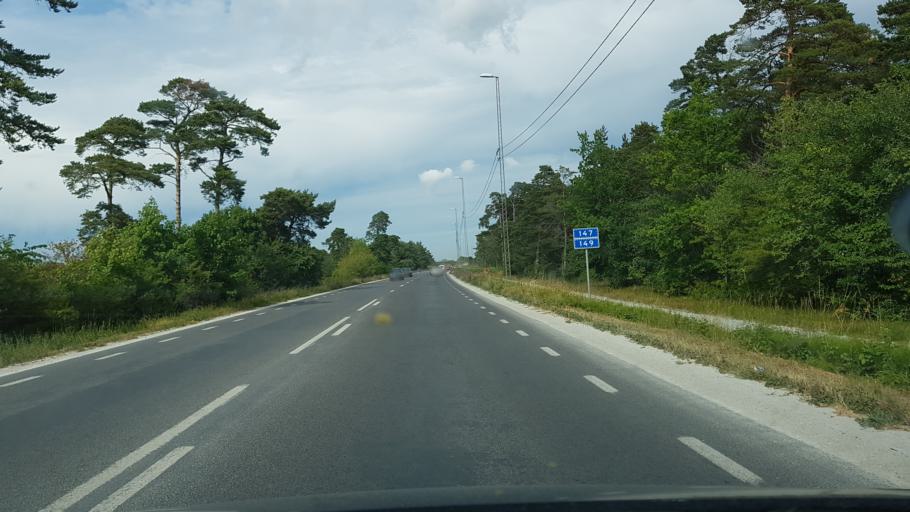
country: SE
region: Gotland
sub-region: Gotland
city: Visby
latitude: 57.6265
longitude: 18.3223
